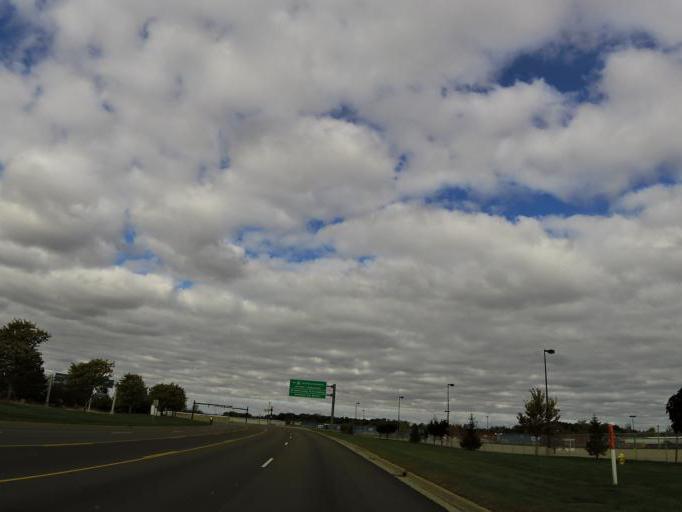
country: US
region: Michigan
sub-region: Genesee County
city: Flint
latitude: 42.9753
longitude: -83.7385
